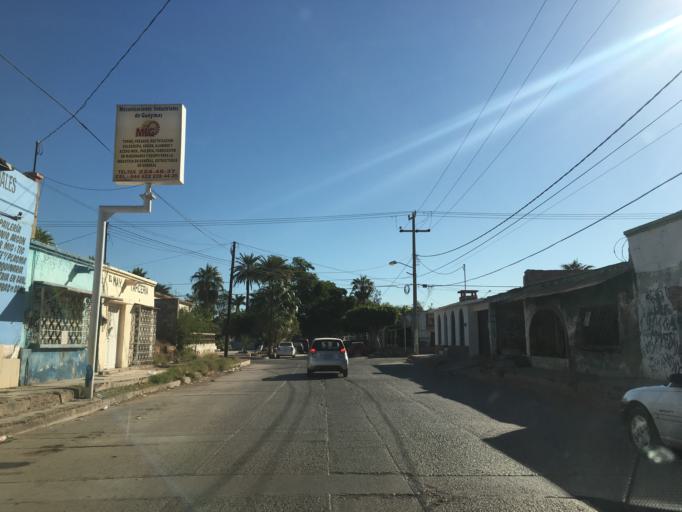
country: MX
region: Sonora
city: Heroica Guaymas
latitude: 27.9178
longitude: -110.8958
